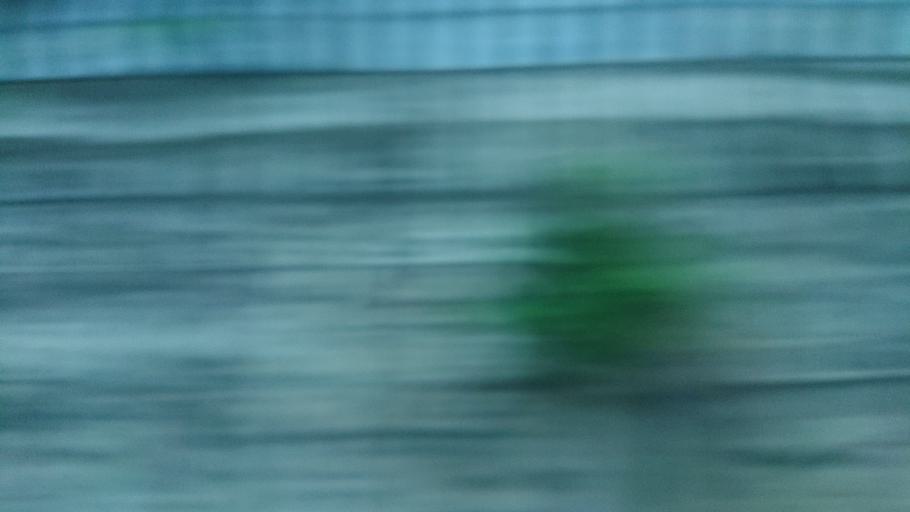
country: TW
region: Taiwan
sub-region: Hualien
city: Hualian
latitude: 24.2184
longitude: 121.6894
